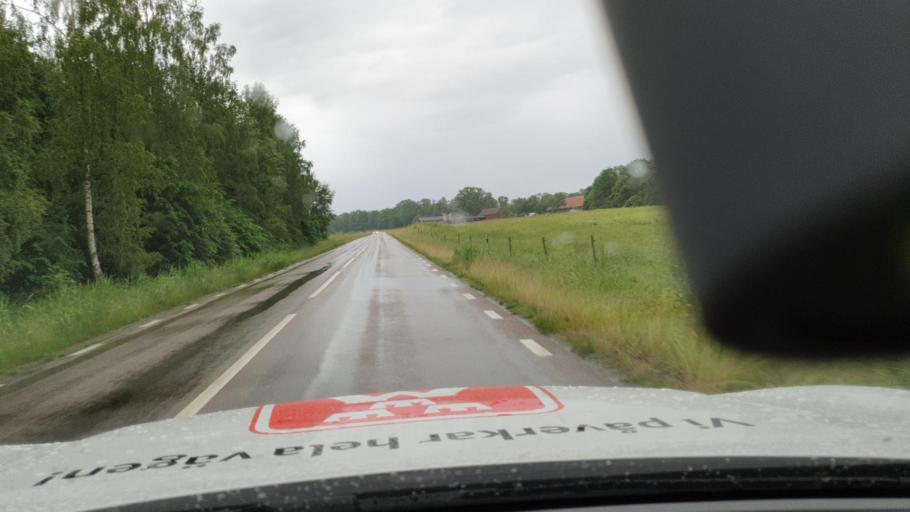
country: SE
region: Vaestra Goetaland
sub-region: Mariestads Kommun
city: Mariestad
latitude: 58.7525
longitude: 13.9090
